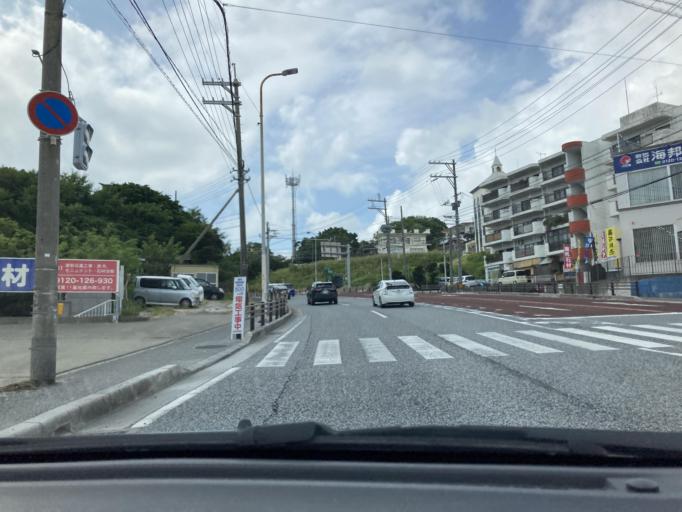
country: JP
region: Okinawa
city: Okinawa
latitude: 26.3178
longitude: 127.8197
